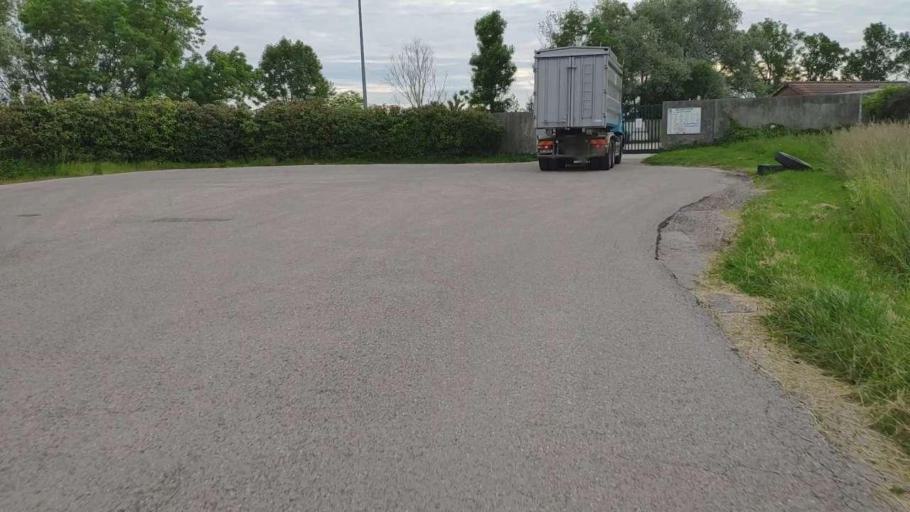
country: FR
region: Franche-Comte
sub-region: Departement du Jura
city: Bletterans
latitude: 46.7511
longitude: 5.4631
